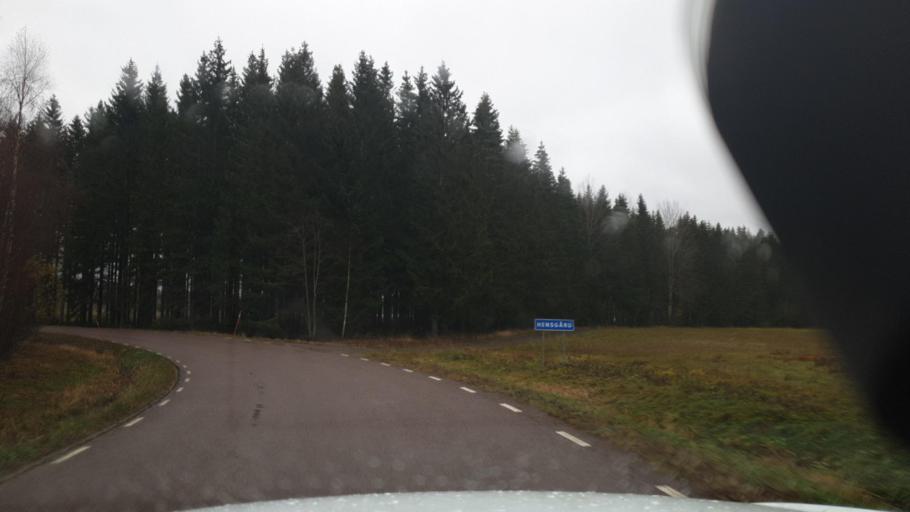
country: SE
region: Vaermland
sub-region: Sunne Kommun
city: Sunne
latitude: 59.7401
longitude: 13.0666
